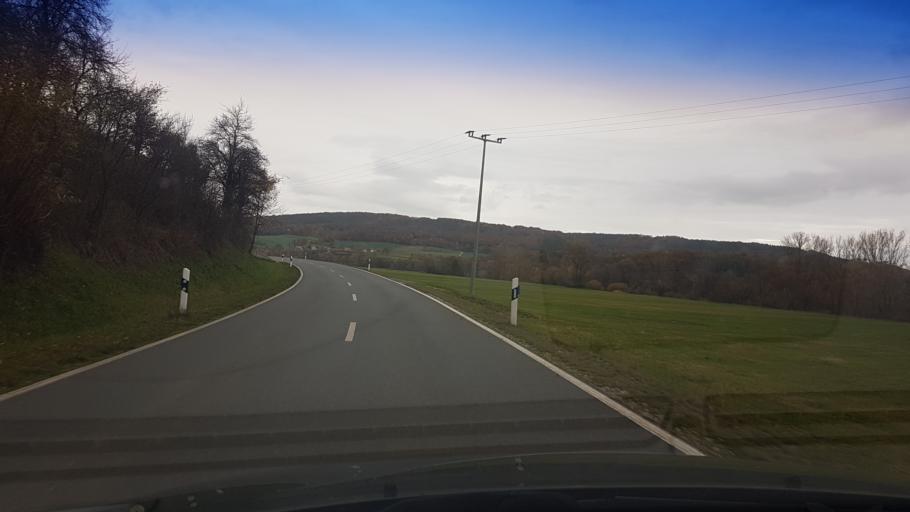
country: DE
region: Bavaria
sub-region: Upper Franconia
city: Rattelsdorf
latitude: 50.0499
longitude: 10.8730
